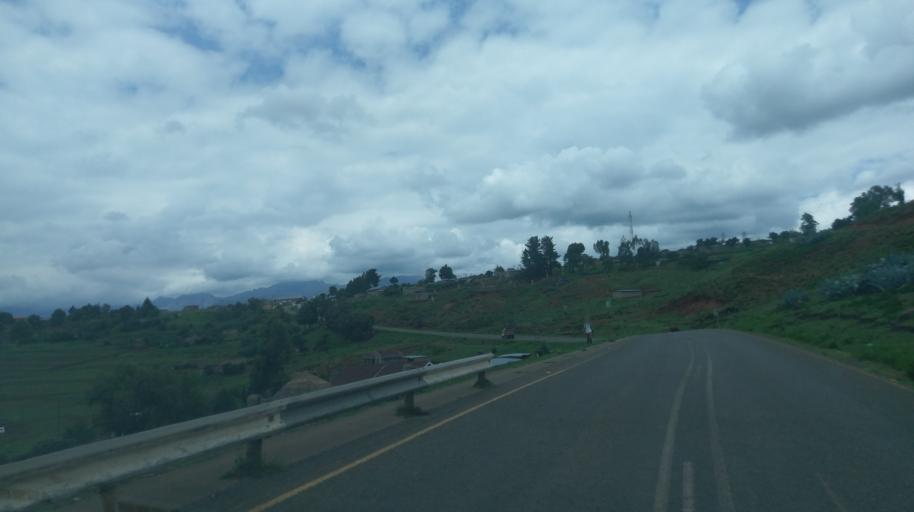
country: LS
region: Leribe
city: Leribe
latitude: -28.9971
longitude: 28.2044
